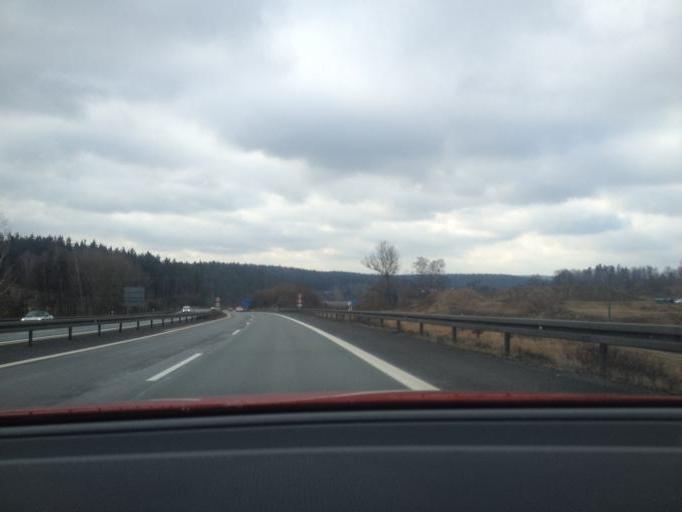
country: DE
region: Bavaria
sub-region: Upper Franconia
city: Selb
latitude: 50.1660
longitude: 12.1073
